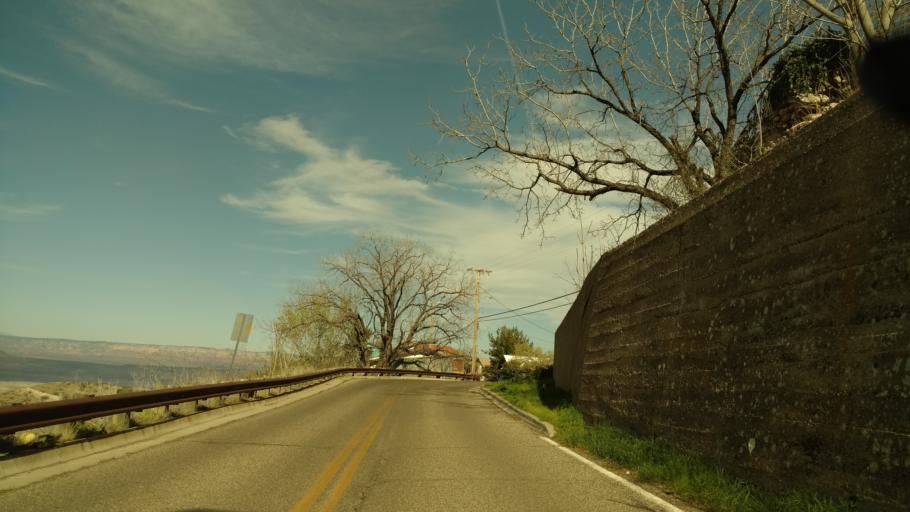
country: US
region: Arizona
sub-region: Yavapai County
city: Clarkdale
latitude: 34.7491
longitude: -112.1097
